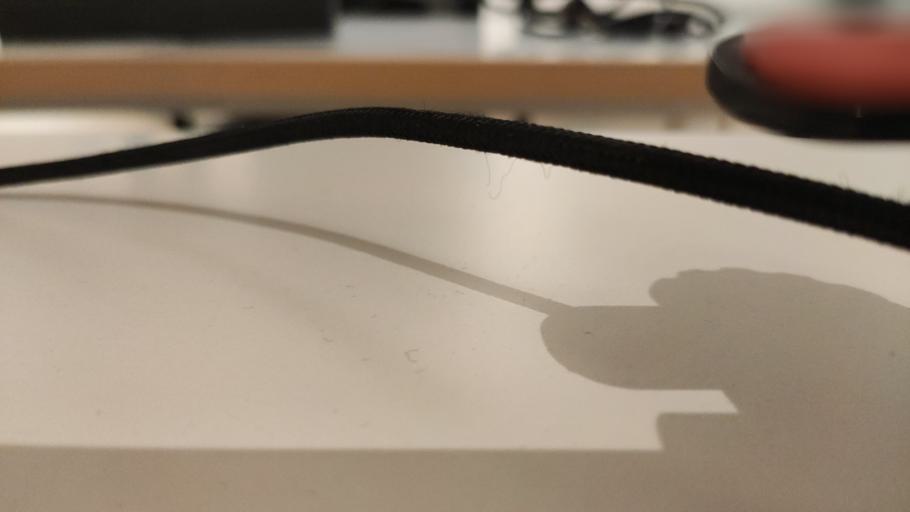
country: RU
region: Kaluga
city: Borovsk
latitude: 55.3676
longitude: 36.4145
